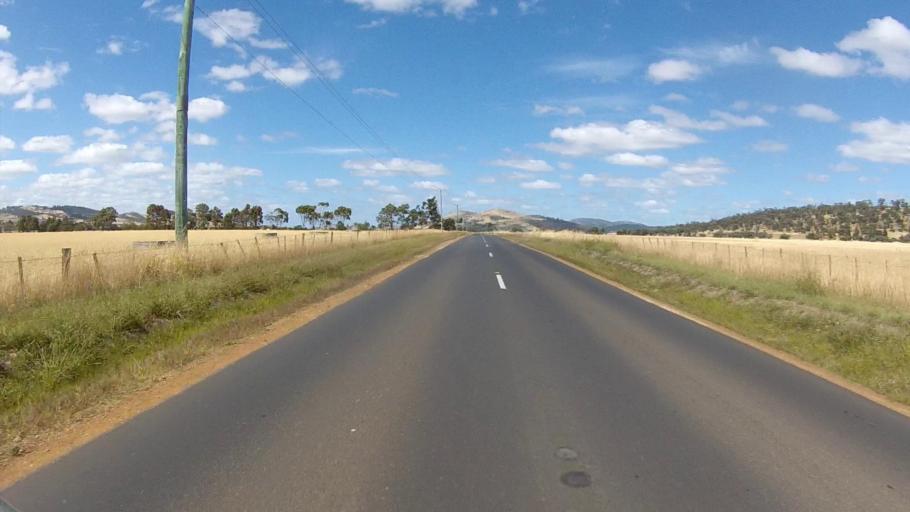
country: AU
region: Tasmania
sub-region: Clarence
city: Cambridge
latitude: -42.7082
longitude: 147.4298
